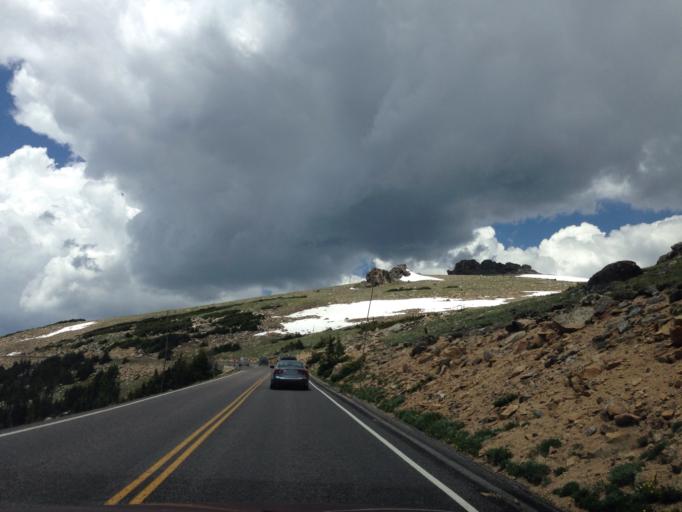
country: US
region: Colorado
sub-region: Larimer County
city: Estes Park
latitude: 40.3939
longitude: -105.6974
